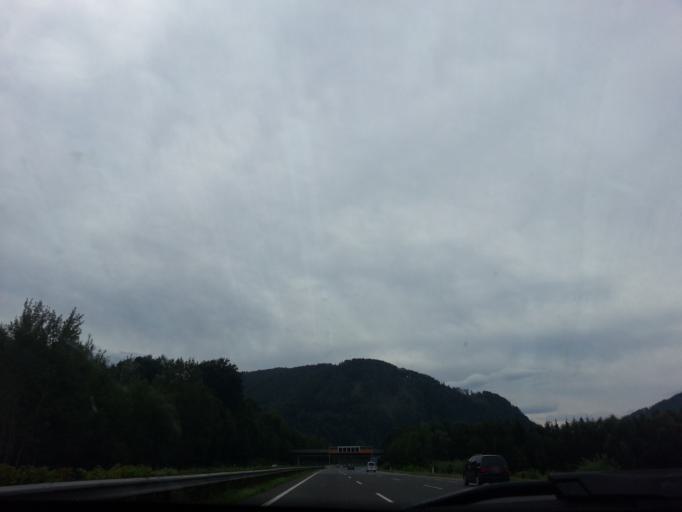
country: AT
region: Styria
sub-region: Politischer Bezirk Graz-Umgebung
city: Deutschfeistritz
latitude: 47.1737
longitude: 15.3320
